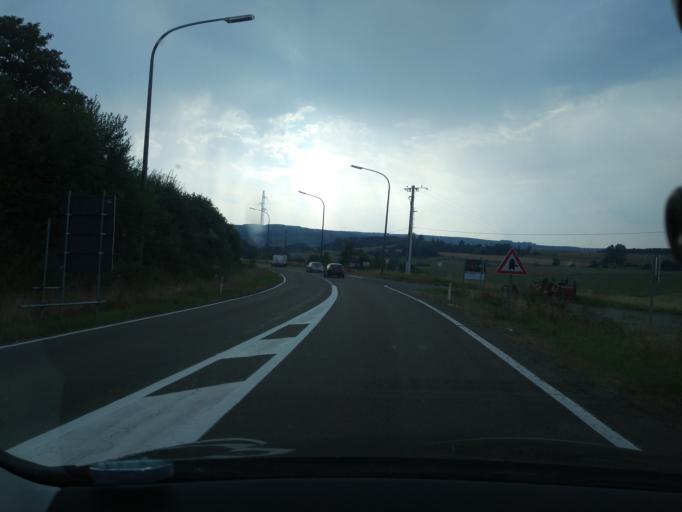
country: BE
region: Wallonia
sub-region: Province du Luxembourg
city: Sainte-Ode
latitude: 50.0443
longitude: 5.5627
